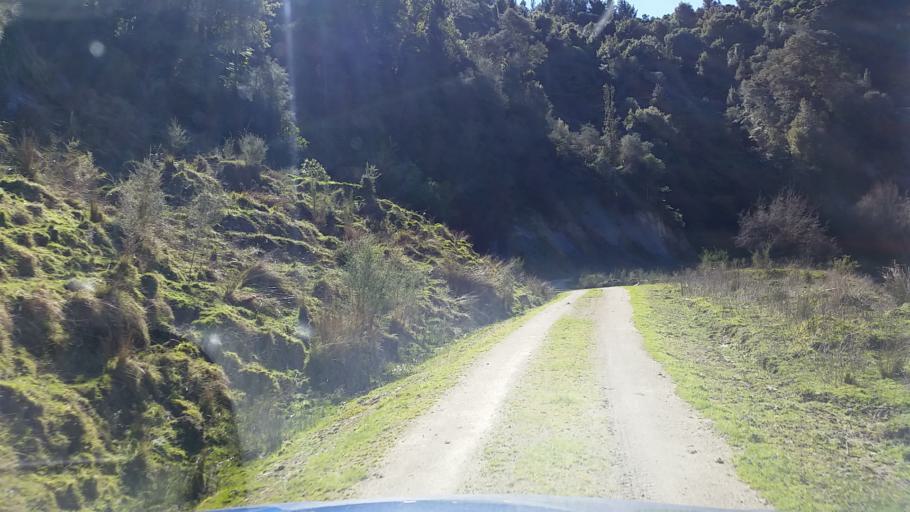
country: NZ
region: Manawatu-Wanganui
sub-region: Wanganui District
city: Wanganui
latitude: -39.6659
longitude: 174.8555
